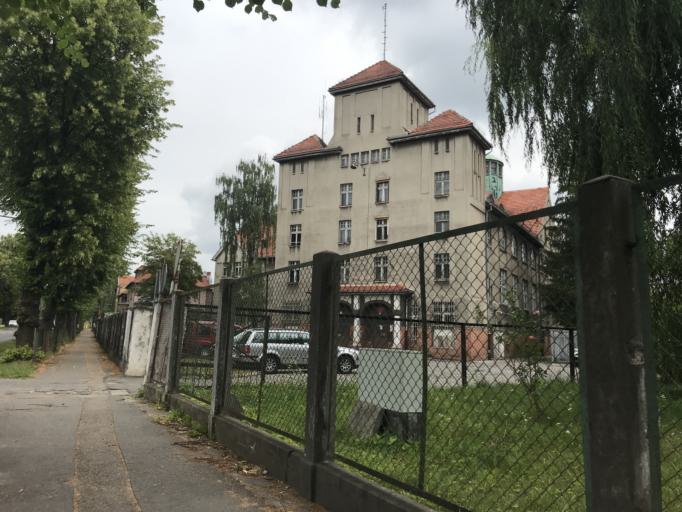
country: PL
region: Warmian-Masurian Voivodeship
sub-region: Powiat elblaski
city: Elblag
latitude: 54.1691
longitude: 19.4096
